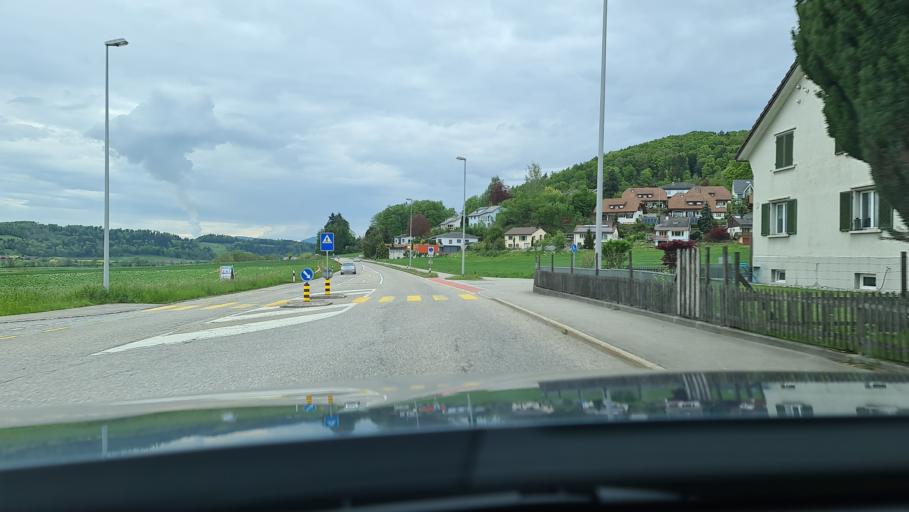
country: CH
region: Aargau
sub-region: Bezirk Zofingen
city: Kirchleerau
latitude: 47.2799
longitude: 8.0608
